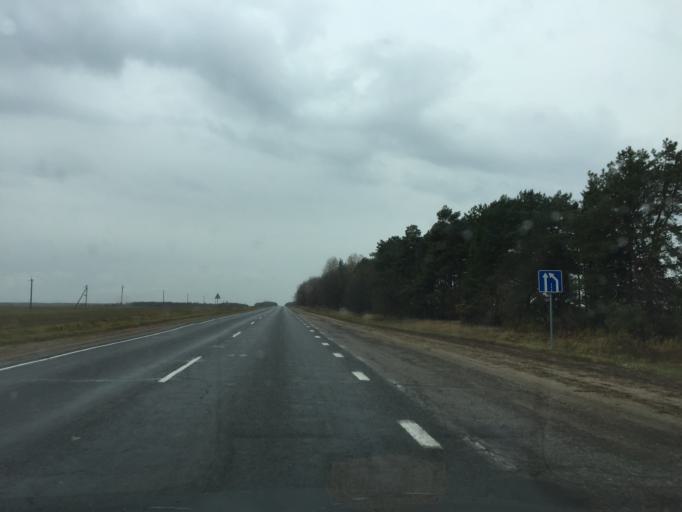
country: BY
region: Mogilev
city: Slawharad
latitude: 53.3942
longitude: 30.9091
